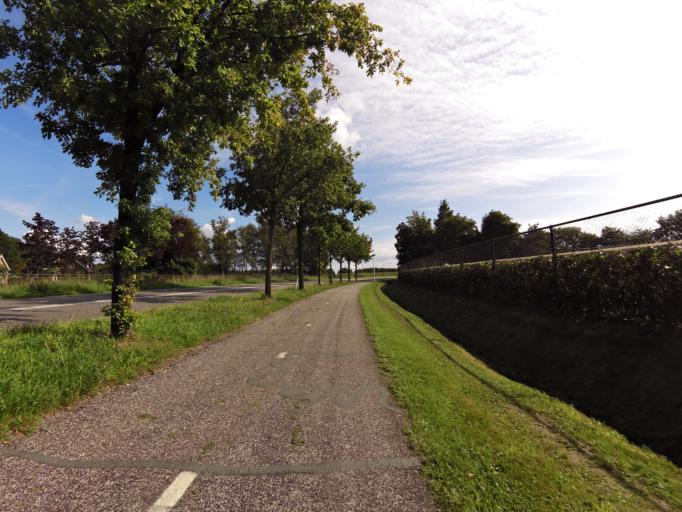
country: NL
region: North Brabant
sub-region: Gemeente Woensdrecht
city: Woensdrecht
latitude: 51.4554
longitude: 4.3767
